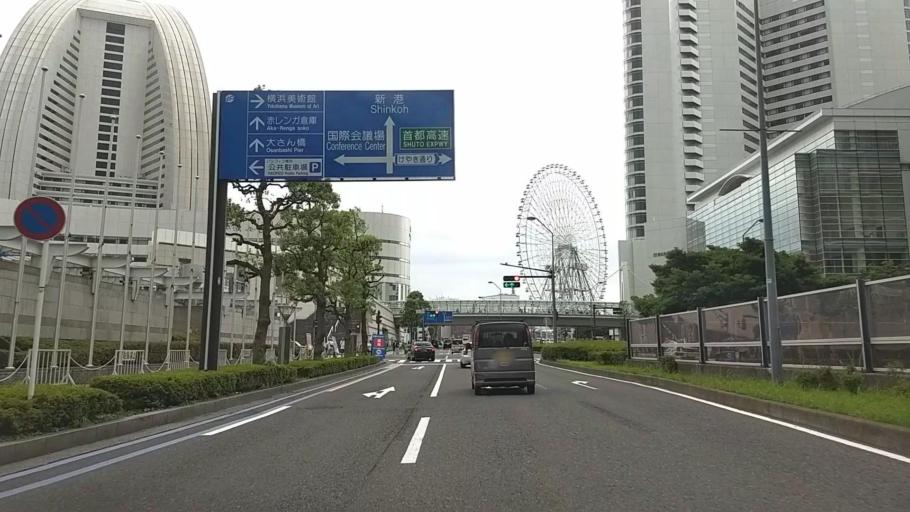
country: JP
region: Kanagawa
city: Yokohama
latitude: 35.4587
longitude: 139.6350
